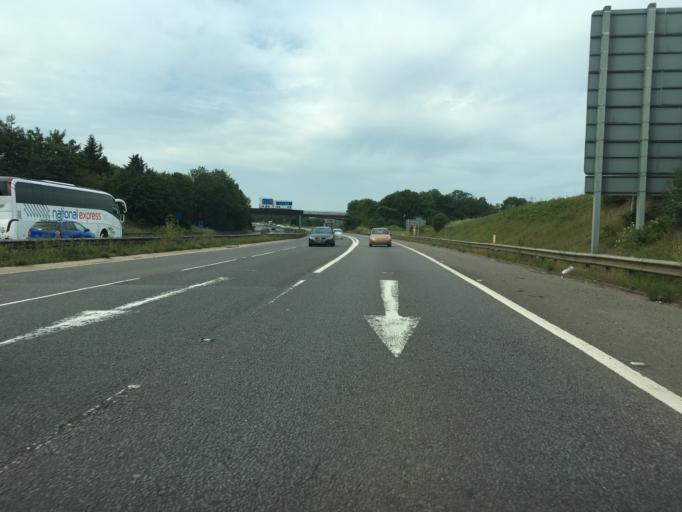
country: GB
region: England
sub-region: South Gloucestershire
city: Stoke Gifford
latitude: 51.5115
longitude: -2.5214
